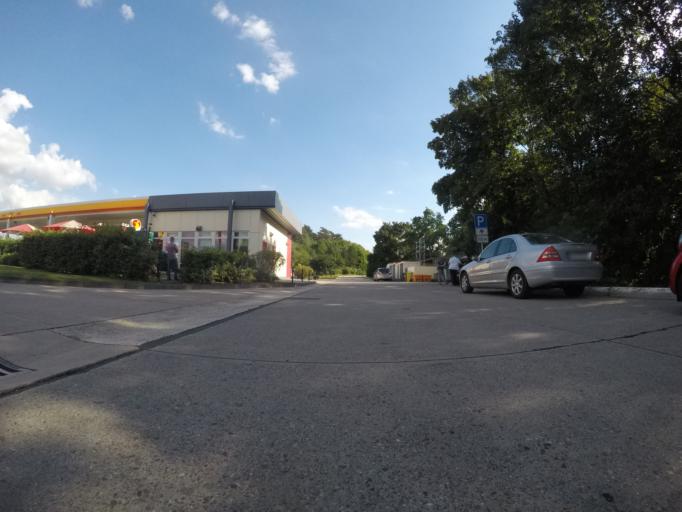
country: DE
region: Baden-Wuerttemberg
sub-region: Regierungsbezirk Stuttgart
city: Grunsfeld
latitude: 49.6286
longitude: 9.7285
